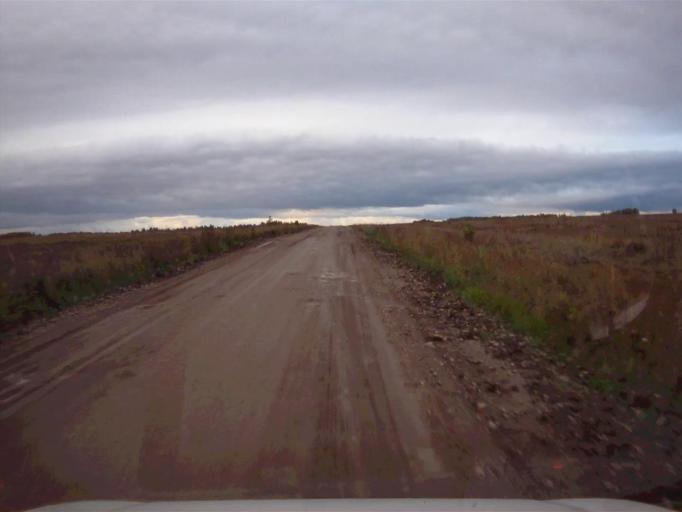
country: RU
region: Sverdlovsk
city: Mikhaylovsk
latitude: 56.1831
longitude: 59.1847
